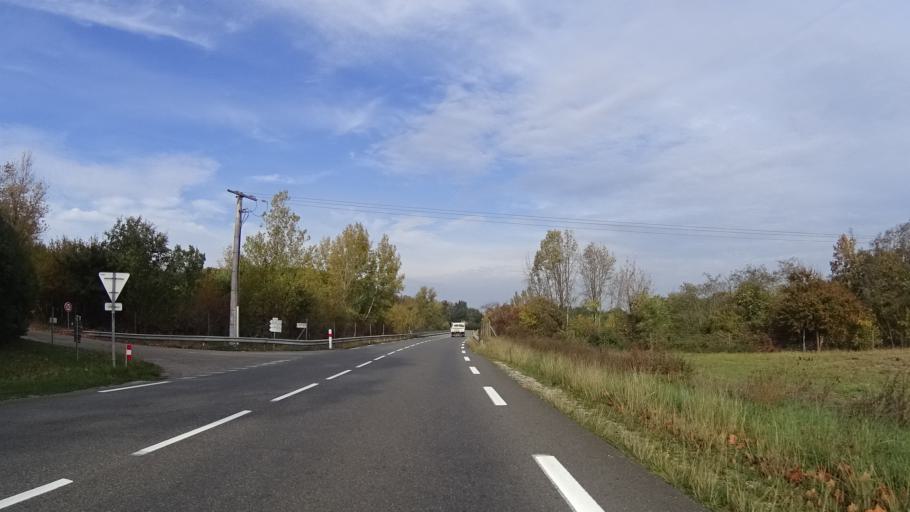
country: FR
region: Aquitaine
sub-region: Departement du Lot-et-Garonne
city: Layrac
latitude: 44.1410
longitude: 0.6485
